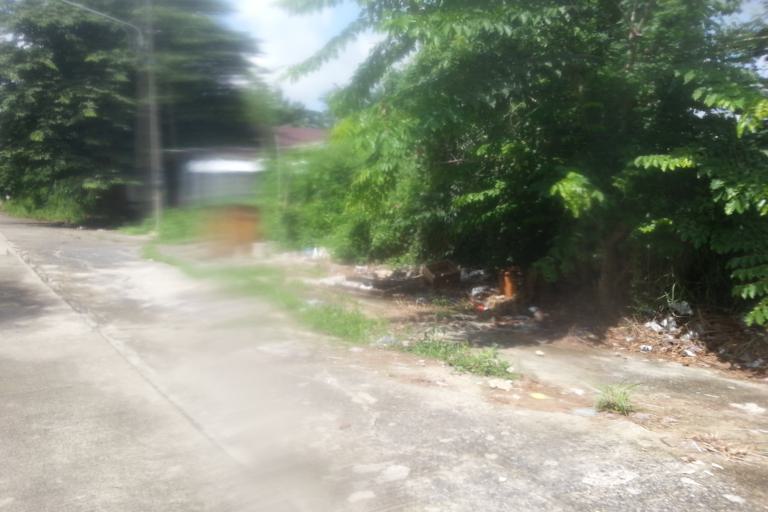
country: TH
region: Pathum Thani
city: Nong Suea
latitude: 14.0565
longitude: 100.8628
